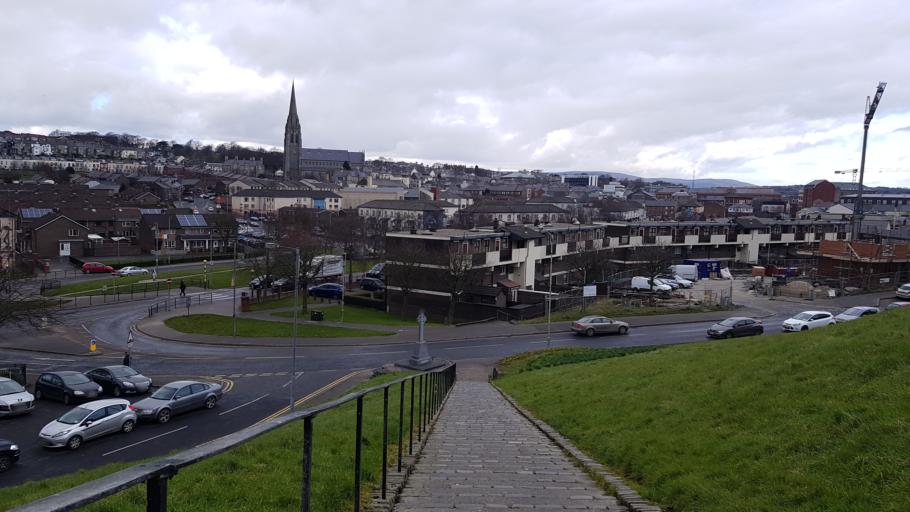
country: GB
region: Northern Ireland
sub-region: City of Derry
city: Derry
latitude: 54.9952
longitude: -7.3259
